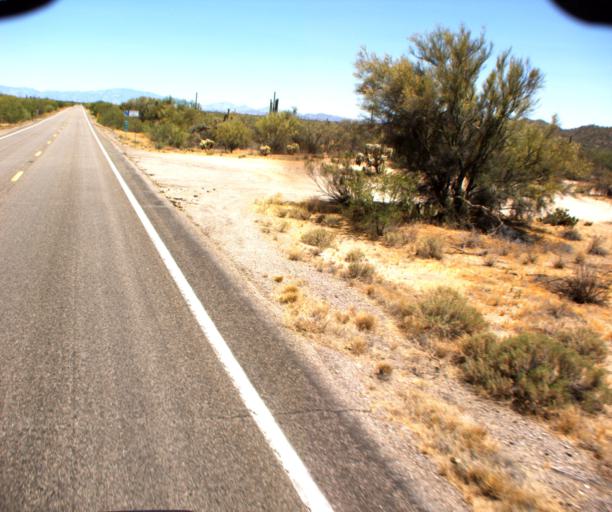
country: US
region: Arizona
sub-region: Pima County
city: Marana
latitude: 32.7591
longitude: -111.1444
